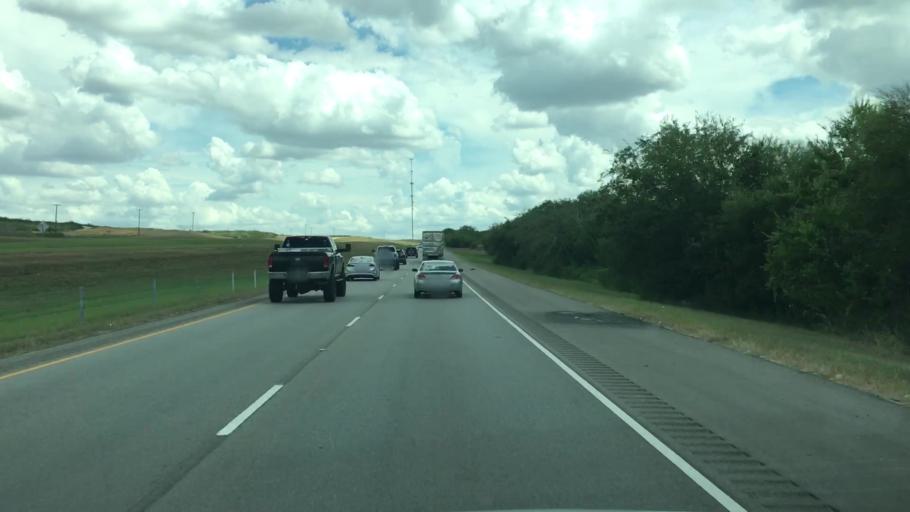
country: US
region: Texas
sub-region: San Patricio County
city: Mathis
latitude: 28.2609
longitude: -97.9294
